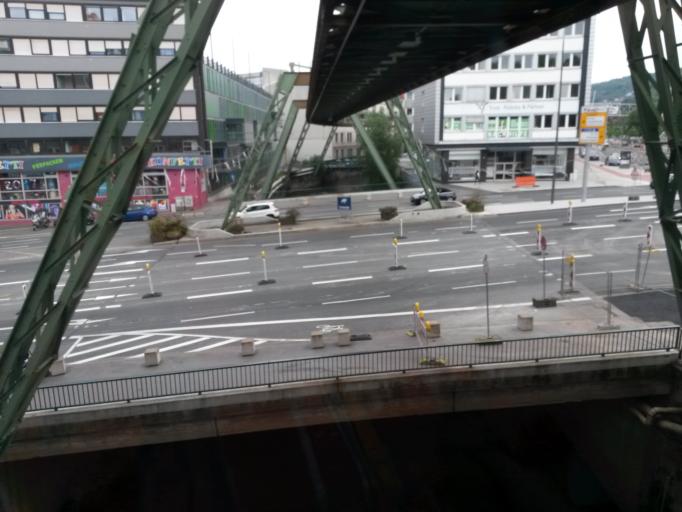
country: DE
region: North Rhine-Westphalia
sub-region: Regierungsbezirk Dusseldorf
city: Wuppertal
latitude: 51.2566
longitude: 7.1499
